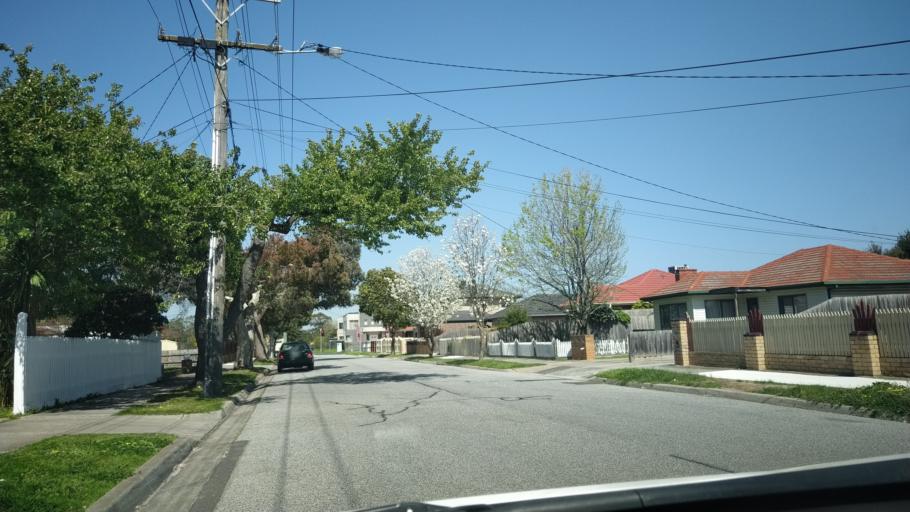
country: AU
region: Victoria
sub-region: Greater Dandenong
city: Noble Park
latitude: -37.9714
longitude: 145.1604
